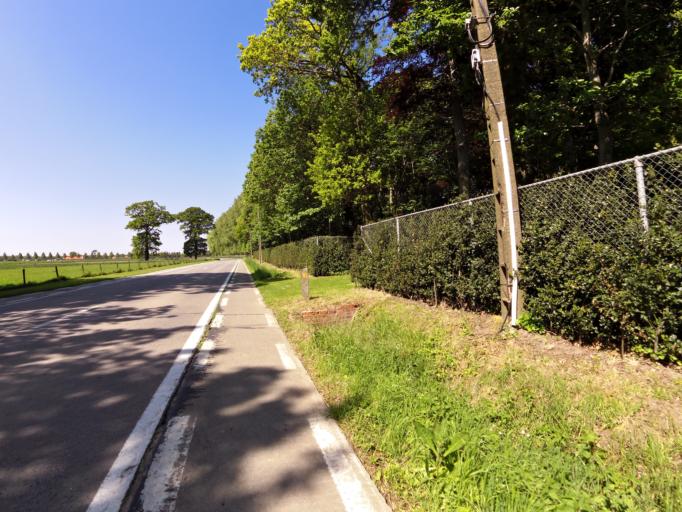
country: BE
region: Flanders
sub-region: Provincie West-Vlaanderen
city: Koekelare
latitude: 51.0591
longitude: 2.9393
